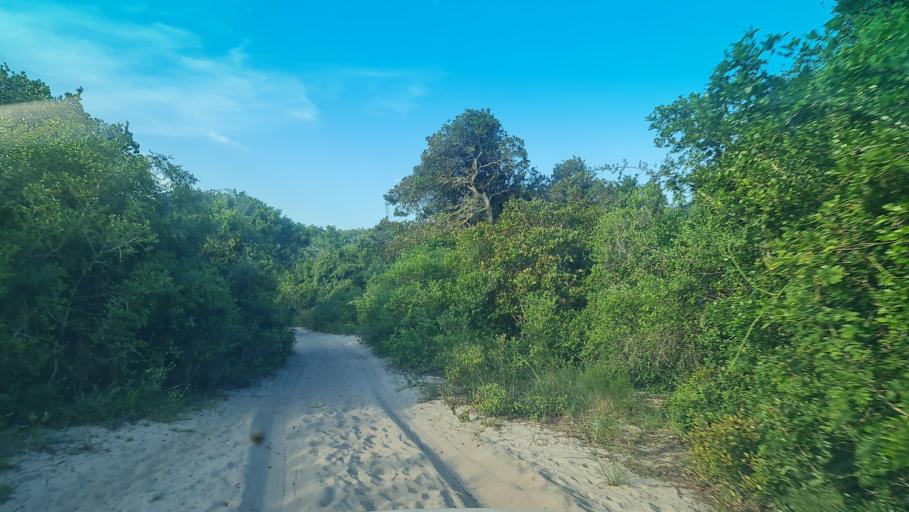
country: MZ
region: Gaza
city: Macia
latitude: -25.2307
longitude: 33.0143
